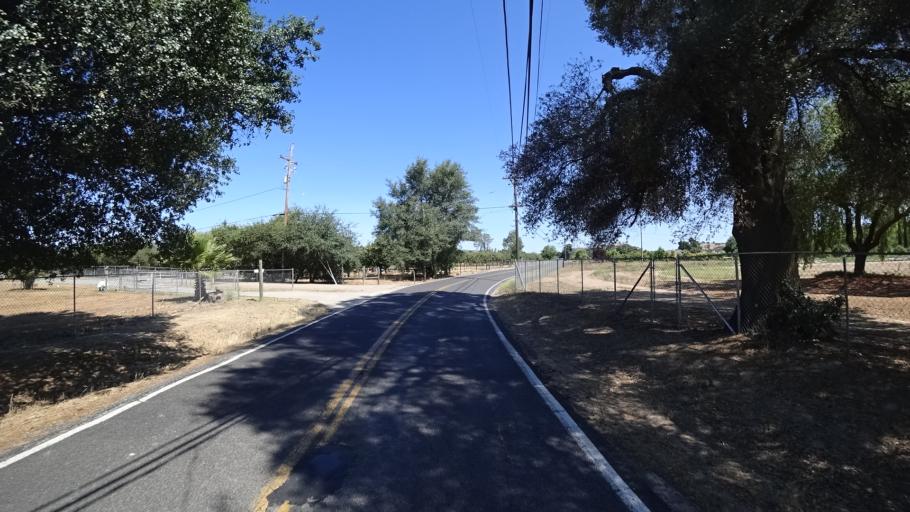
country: US
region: California
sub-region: Calaveras County
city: Rancho Calaveras
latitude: 38.1744
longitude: -120.8907
